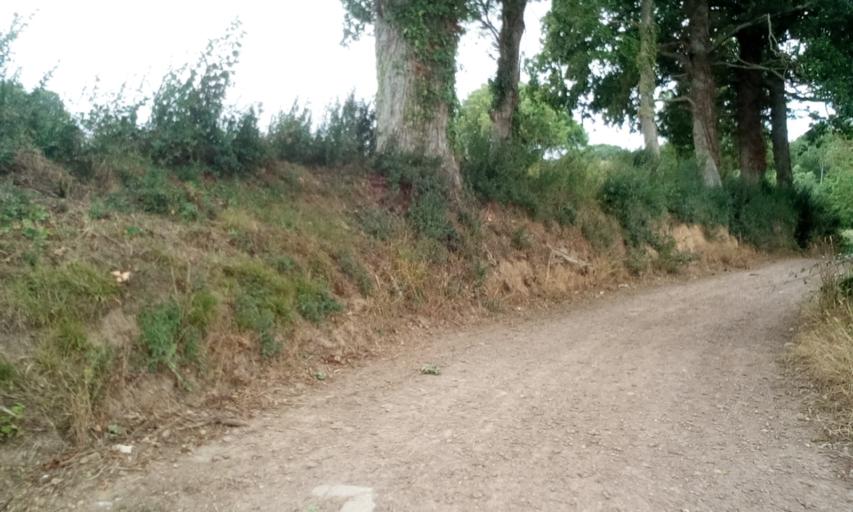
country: FR
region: Lower Normandy
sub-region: Departement du Calvados
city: Tourville-sur-Odon
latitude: 49.1378
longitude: -0.4946
